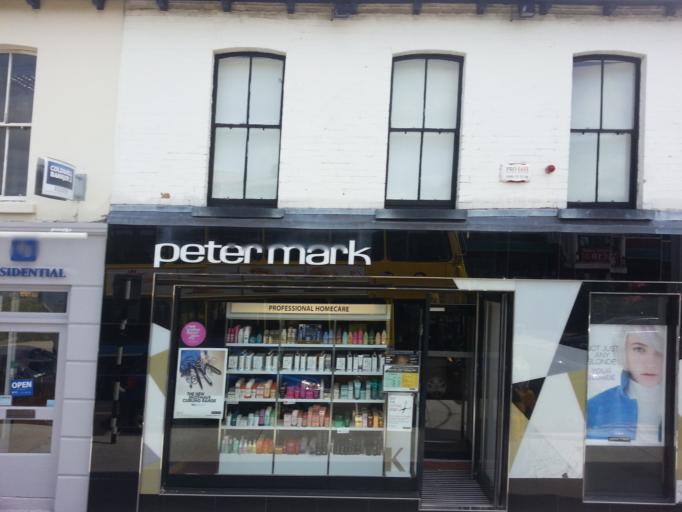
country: IE
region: Leinster
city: Dundrum
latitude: 53.2916
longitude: -6.2457
